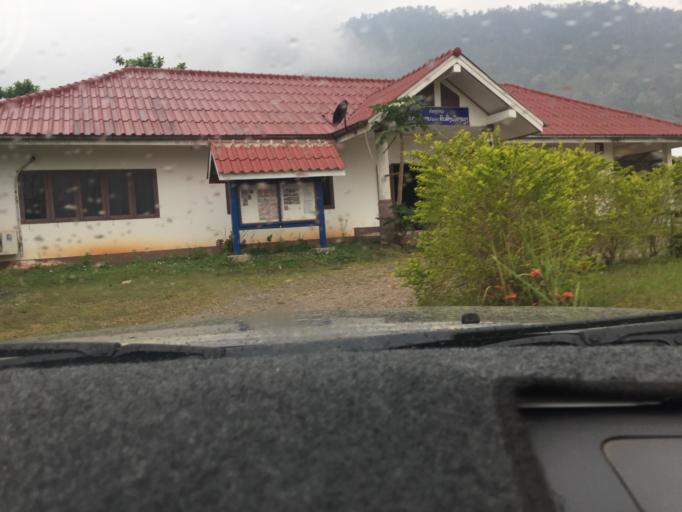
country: LA
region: Xiagnabouli
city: Sainyabuli
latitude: 18.9232
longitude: 101.5100
